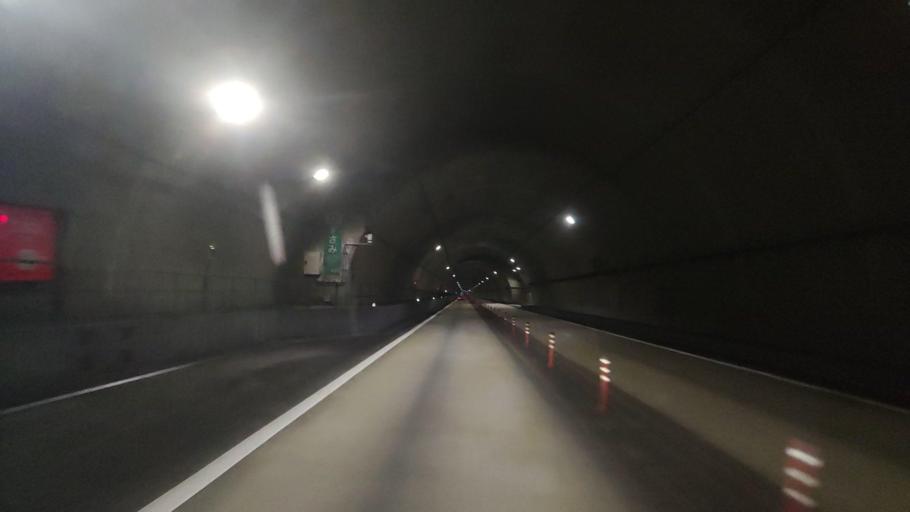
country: JP
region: Wakayama
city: Tanabe
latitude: 33.5456
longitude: 135.5221
